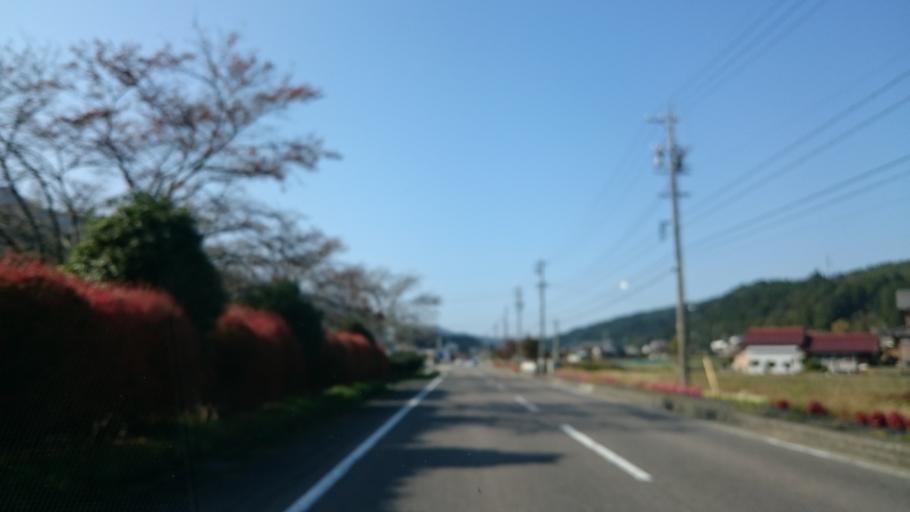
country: JP
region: Gifu
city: Nakatsugawa
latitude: 35.7123
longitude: 137.3709
